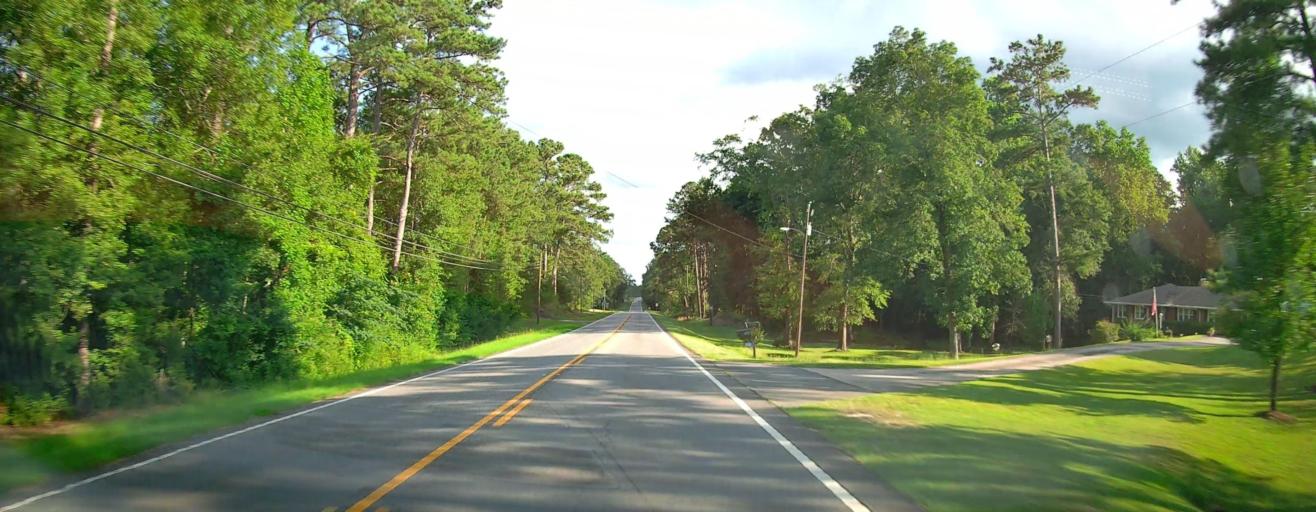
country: US
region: Georgia
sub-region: Crawford County
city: Roberta
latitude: 32.7114
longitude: -84.0103
